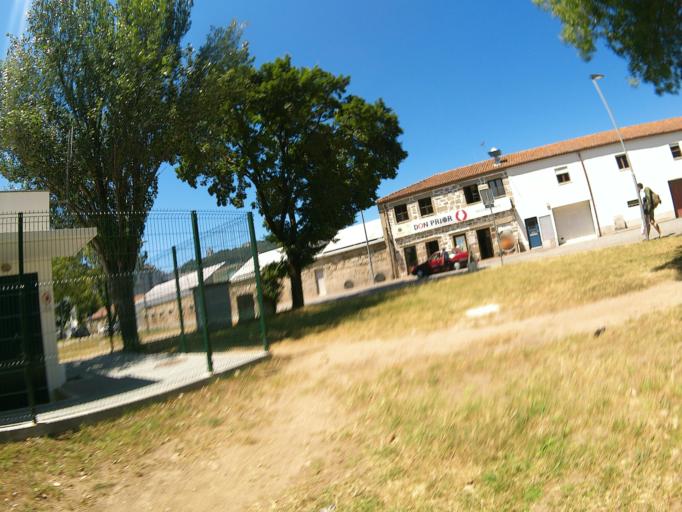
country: PT
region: Viana do Castelo
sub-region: Viana do Castelo
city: Viana do Castelo
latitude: 41.6967
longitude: -8.8175
